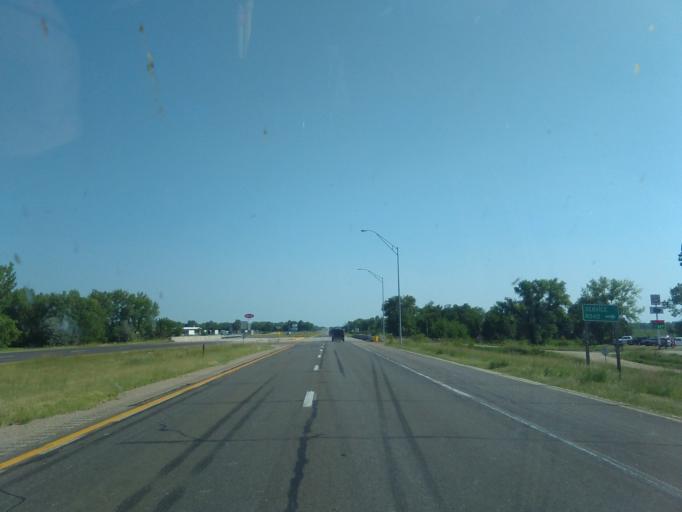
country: US
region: Nebraska
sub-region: Hall County
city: Grand Island
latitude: 40.8165
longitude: -98.3785
